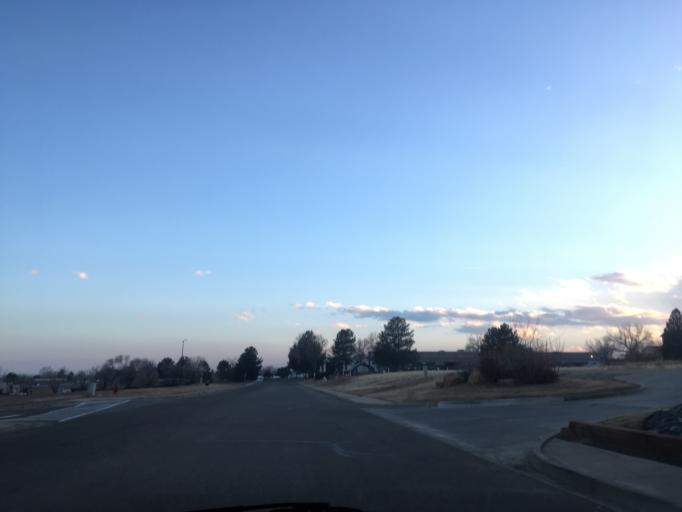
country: US
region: Colorado
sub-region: Boulder County
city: Lafayette
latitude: 40.0050
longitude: -105.1064
